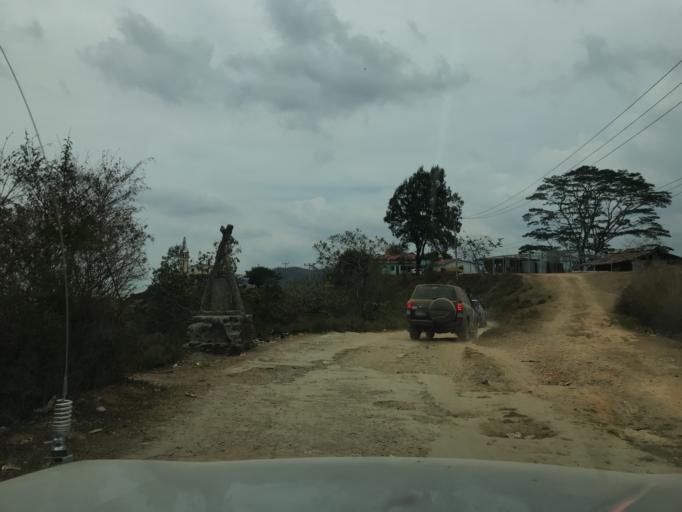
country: TL
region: Ermera
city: Gleno
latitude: -8.8377
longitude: 125.4341
